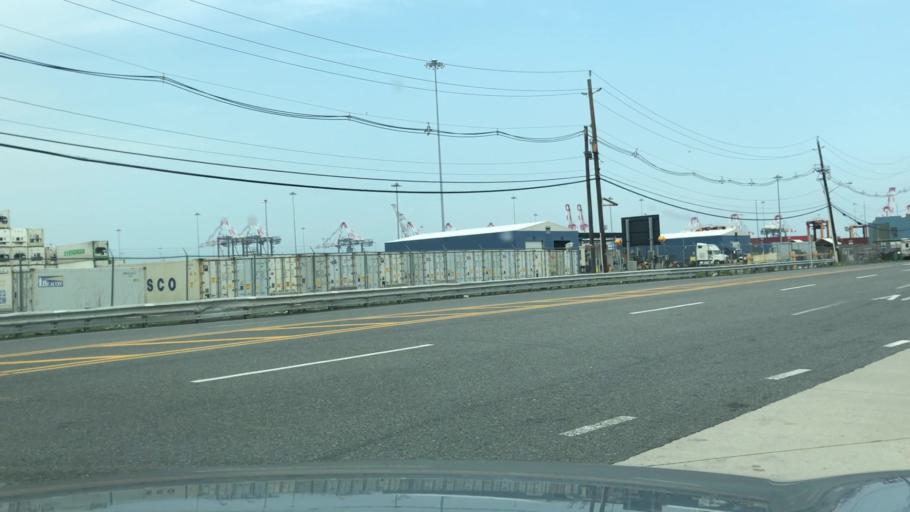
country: US
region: New Jersey
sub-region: Hudson County
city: Bayonne
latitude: 40.6736
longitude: -74.1590
